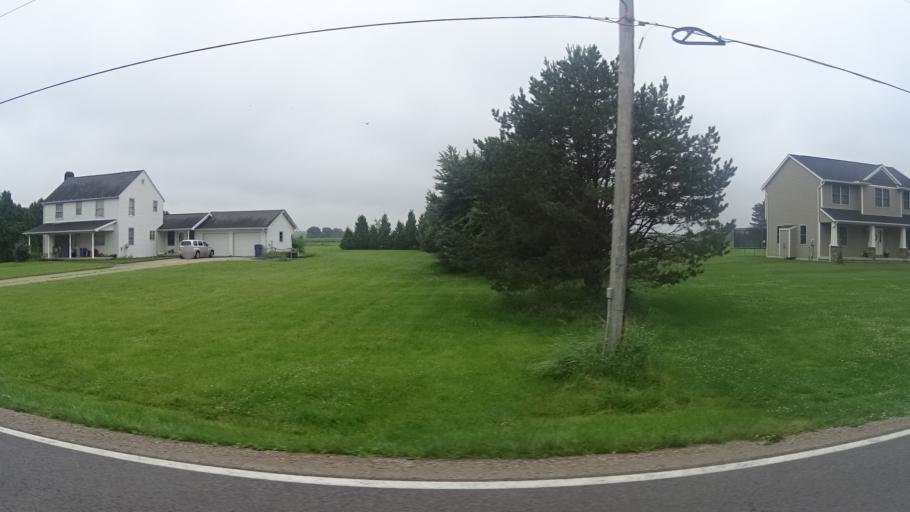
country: US
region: Ohio
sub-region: Erie County
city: Milan
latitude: 41.3588
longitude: -82.6253
